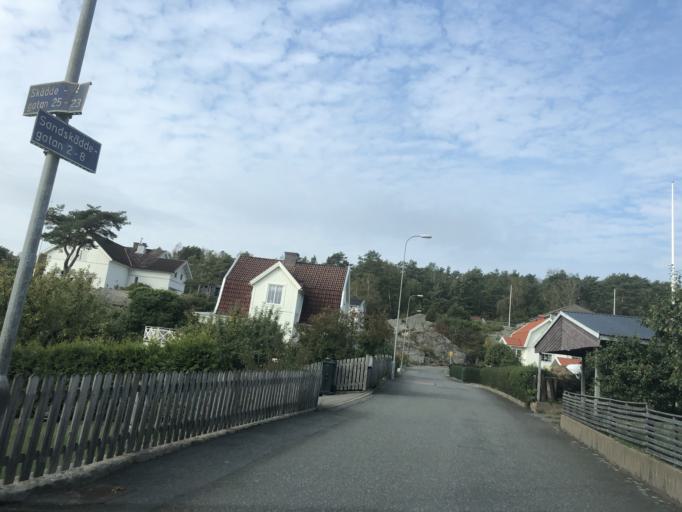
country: SE
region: Vaestra Goetaland
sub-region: Goteborg
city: Majorna
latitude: 57.6536
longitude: 11.8621
